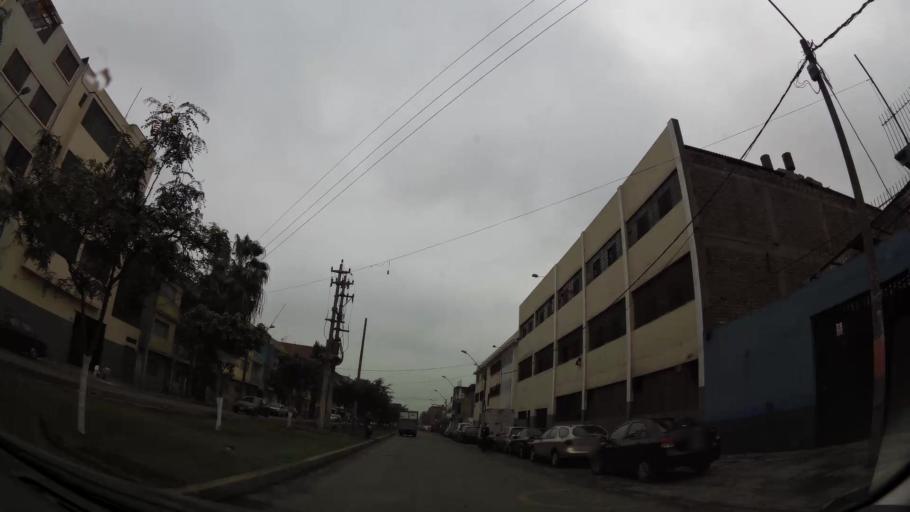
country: PE
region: Lima
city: Lima
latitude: -12.0679
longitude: -77.0199
